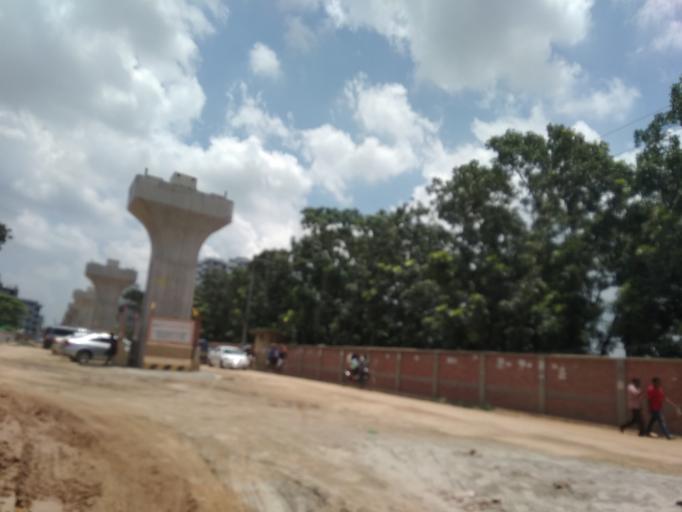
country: BD
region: Dhaka
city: Tungi
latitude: 23.8320
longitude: 90.3637
